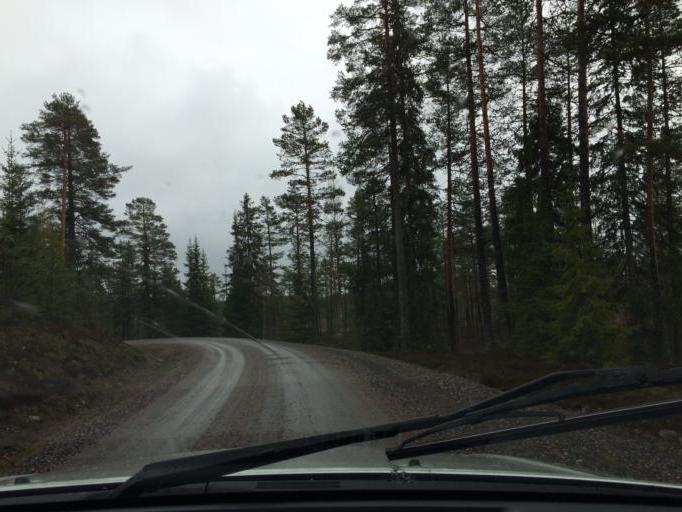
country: SE
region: OErebro
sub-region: Hallefors Kommun
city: Haellefors
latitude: 60.0239
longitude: 14.5606
